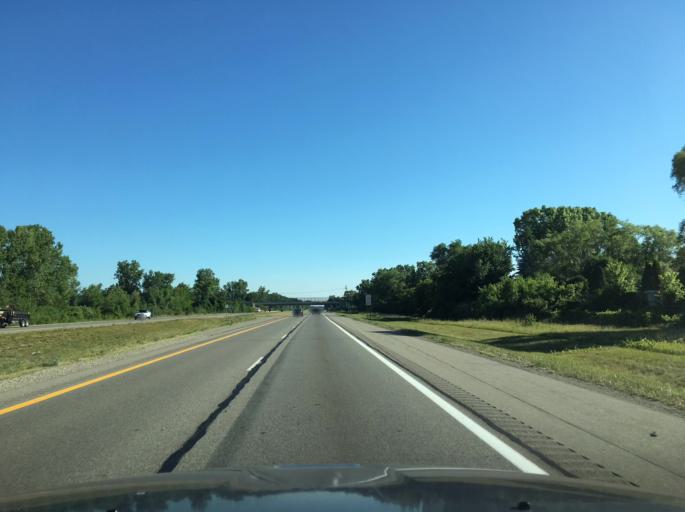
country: US
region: Michigan
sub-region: Macomb County
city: Utica
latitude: 42.6368
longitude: -83.0134
